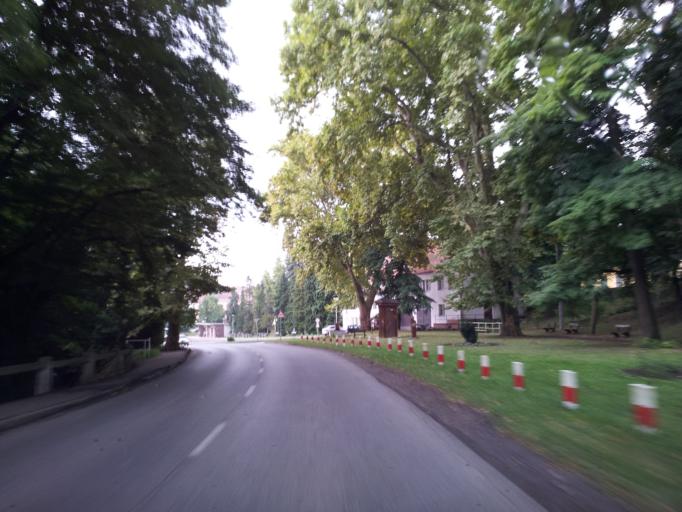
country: HU
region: Tolna
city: Hogyesz
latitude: 46.4979
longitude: 18.4165
